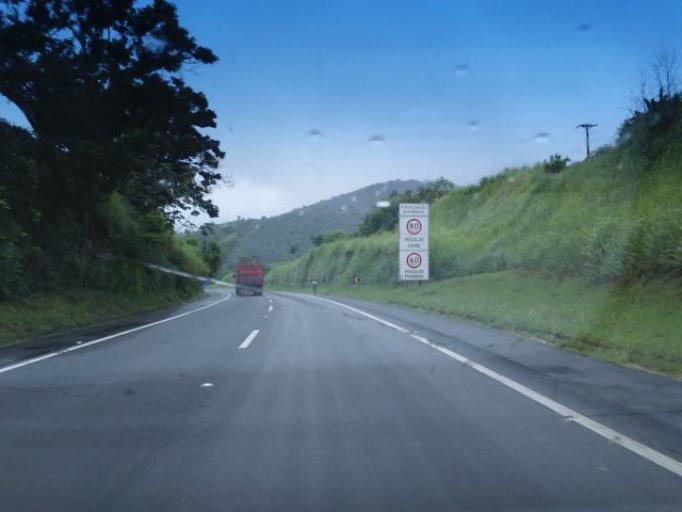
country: BR
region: Sao Paulo
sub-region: Cajati
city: Cajati
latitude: -24.7883
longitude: -48.1792
